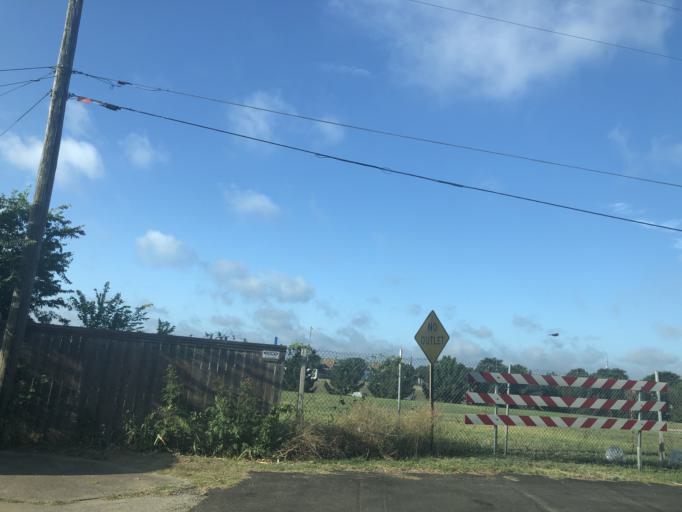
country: US
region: Texas
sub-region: Dallas County
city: Duncanville
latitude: 32.6667
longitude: -96.9096
